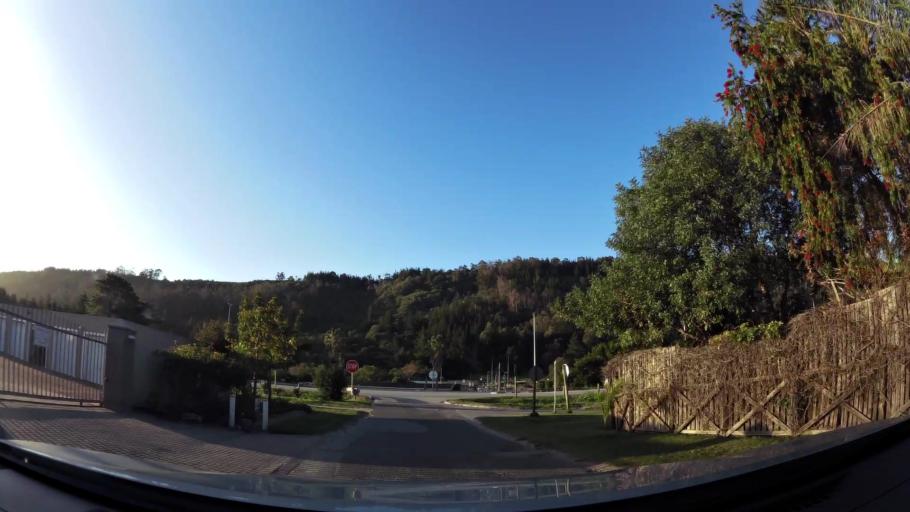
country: ZA
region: Western Cape
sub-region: Eden District Municipality
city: Knysna
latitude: -34.0116
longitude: 22.7946
